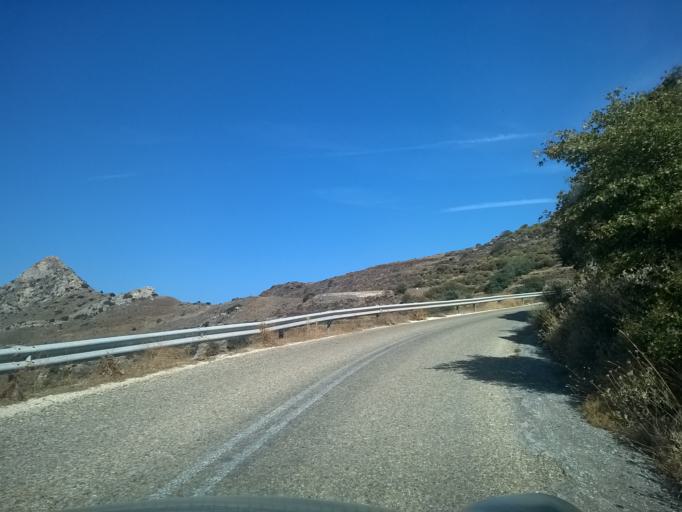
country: GR
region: South Aegean
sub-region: Nomos Kykladon
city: Filotion
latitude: 37.1569
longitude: 25.5511
